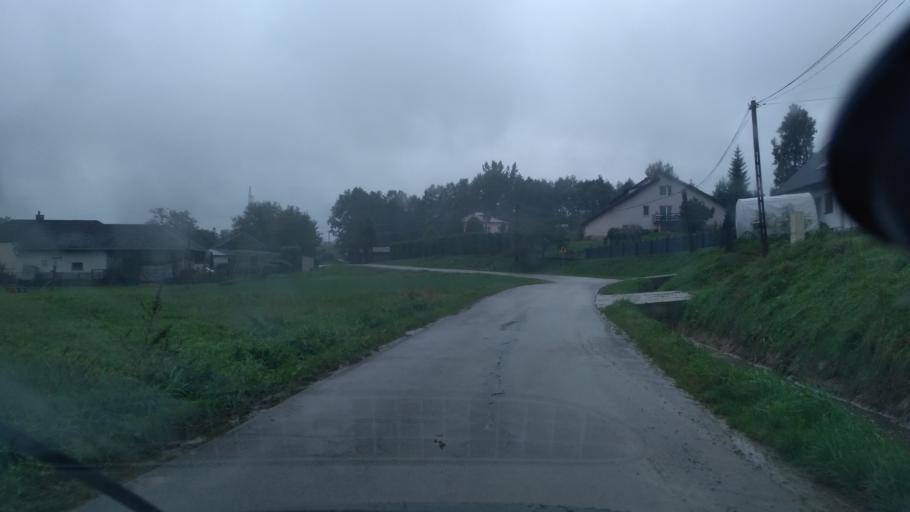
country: PL
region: Subcarpathian Voivodeship
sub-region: Powiat ropczycko-sedziszowski
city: Niedzwiada
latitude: 50.0268
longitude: 21.5417
